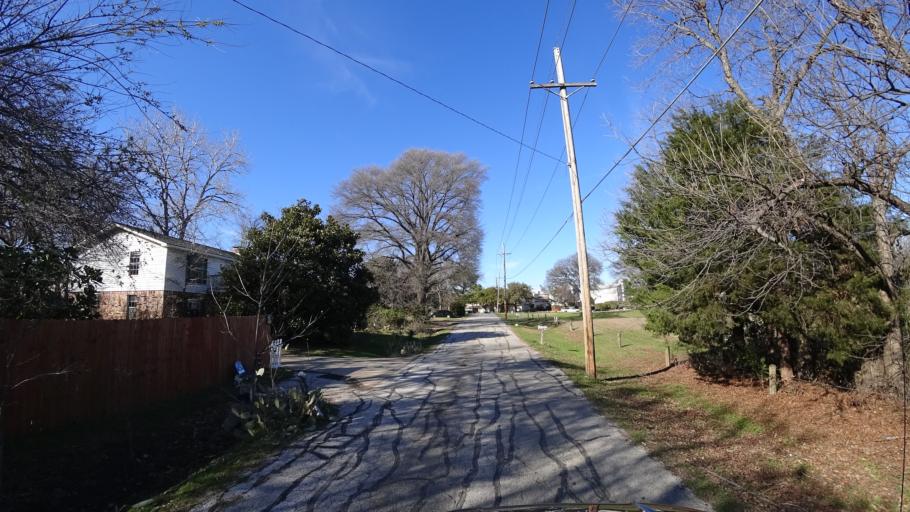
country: US
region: Texas
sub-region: Denton County
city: Highland Village
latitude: 33.0799
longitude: -97.0171
